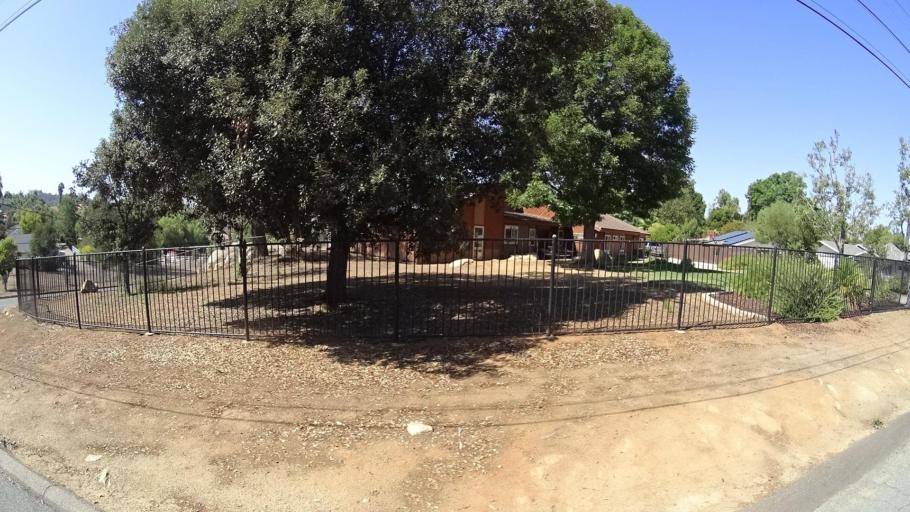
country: US
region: California
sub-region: San Diego County
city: Granite Hills
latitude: 32.7900
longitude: -116.9121
